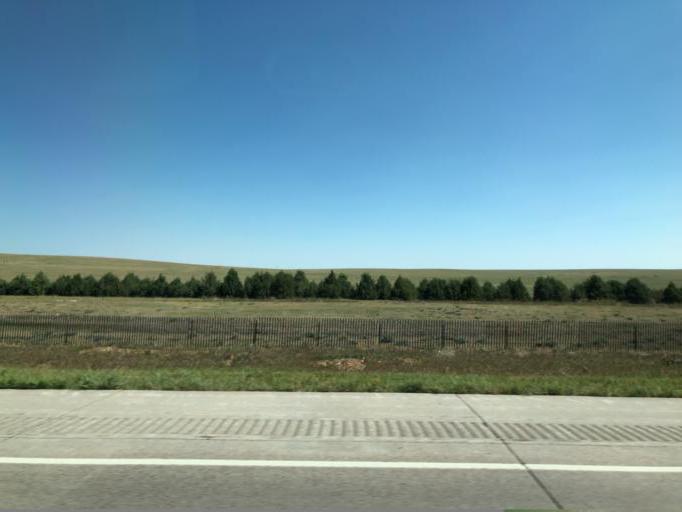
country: US
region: Colorado
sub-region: Lincoln County
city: Limon
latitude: 39.2761
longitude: -103.7470
